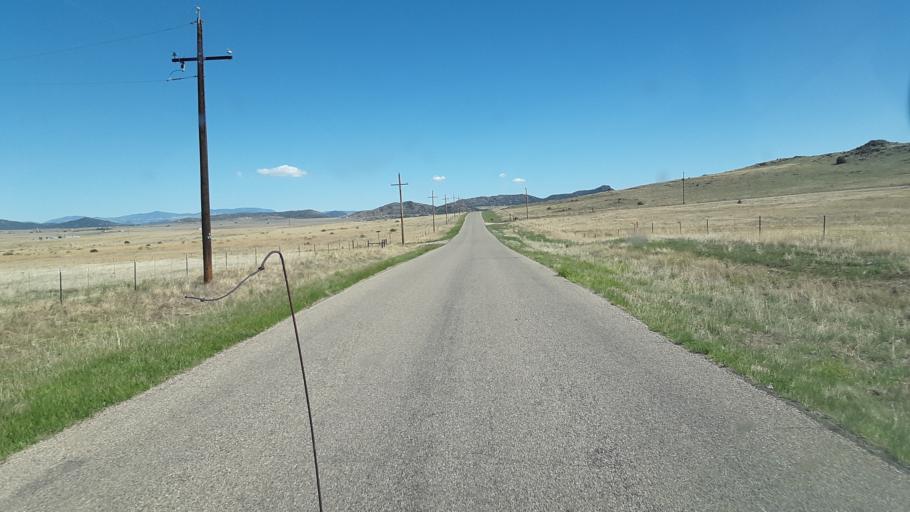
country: US
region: Colorado
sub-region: Custer County
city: Westcliffe
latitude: 38.1753
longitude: -105.4617
